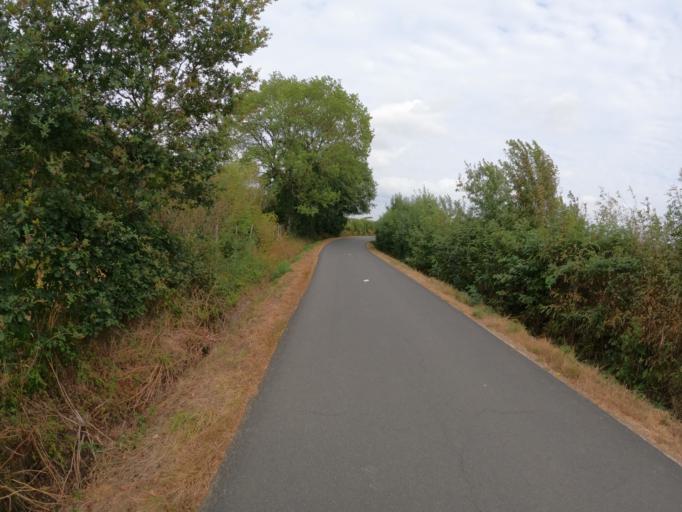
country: FR
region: Pays de la Loire
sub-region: Departement de Maine-et-Loire
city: La Romagne
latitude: 47.0453
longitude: -0.9858
